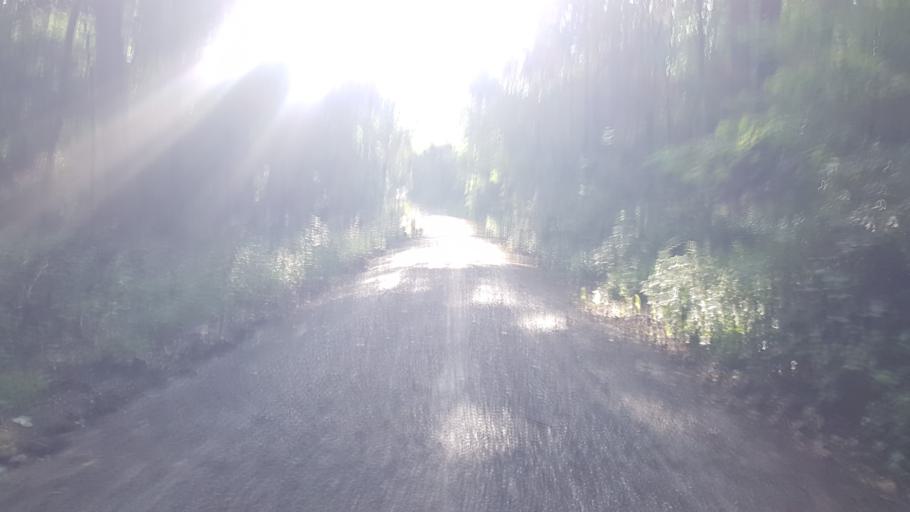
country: DE
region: Baden-Wuerttemberg
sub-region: Regierungsbezirk Stuttgart
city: Zaberfeld
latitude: 49.0439
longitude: 8.8906
